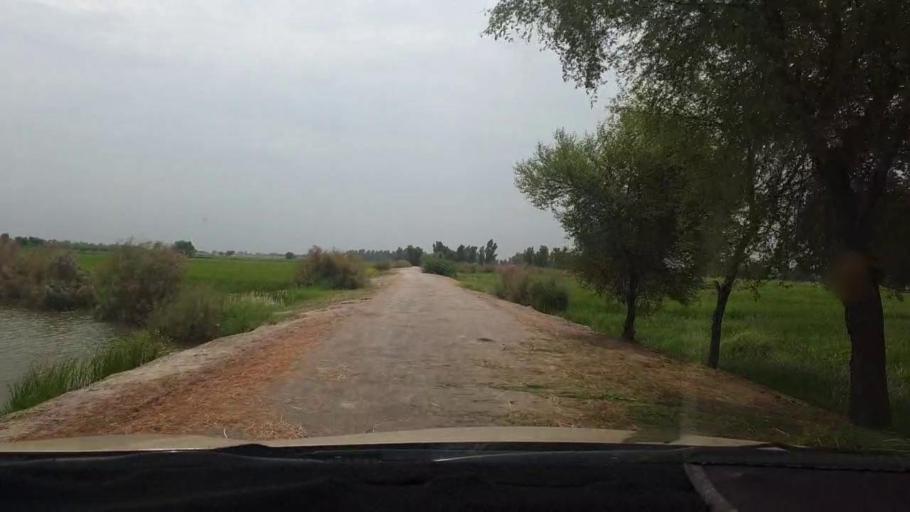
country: PK
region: Sindh
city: Naudero
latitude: 27.6264
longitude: 68.3213
